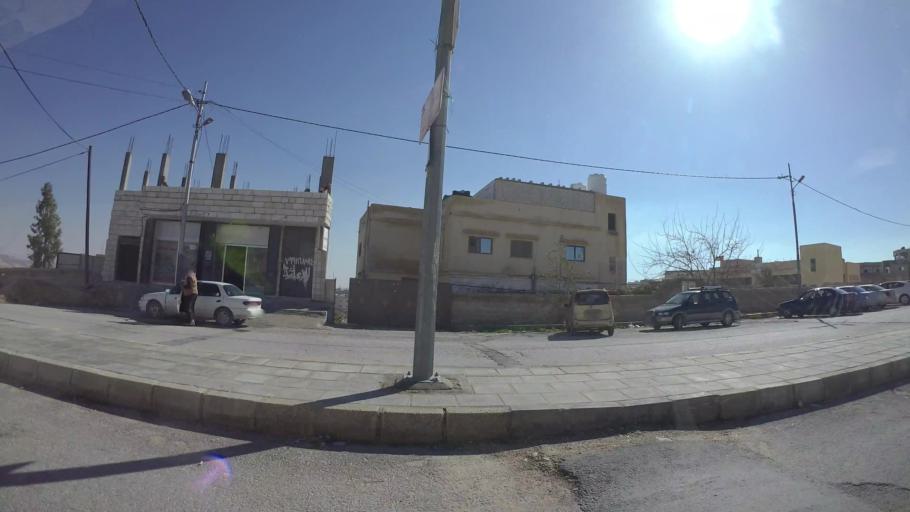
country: JO
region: Zarqa
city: Russeifa
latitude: 32.0428
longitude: 36.0408
